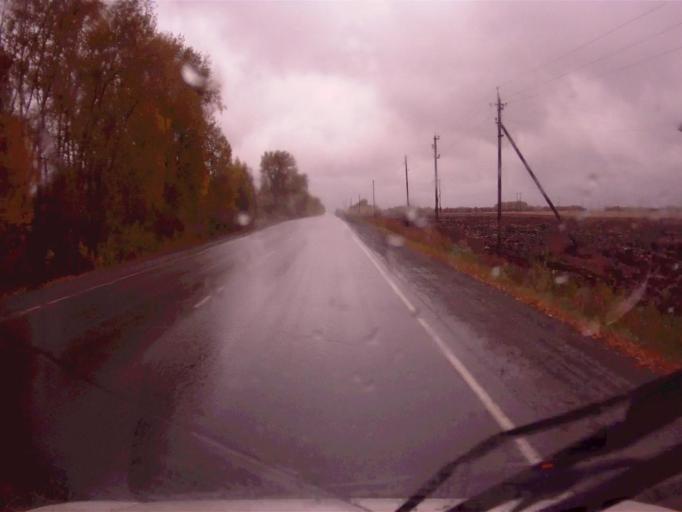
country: RU
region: Chelyabinsk
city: Argayash
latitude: 55.4304
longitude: 60.9909
